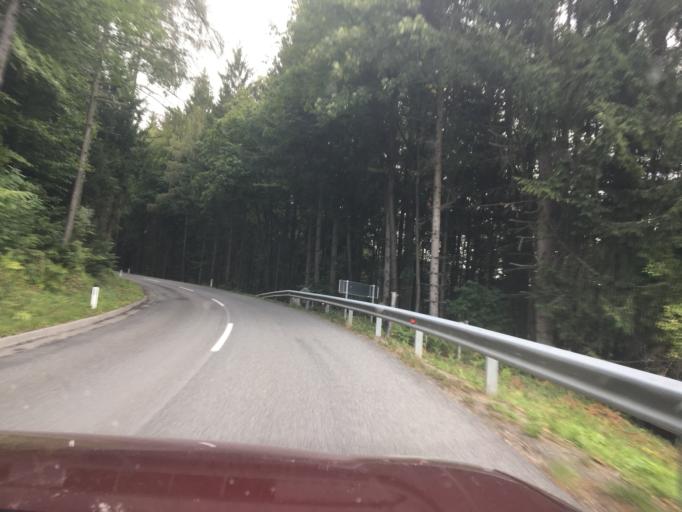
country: AT
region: Styria
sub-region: Politischer Bezirk Deutschlandsberg
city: Hollenegg
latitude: 46.8073
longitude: 15.1879
